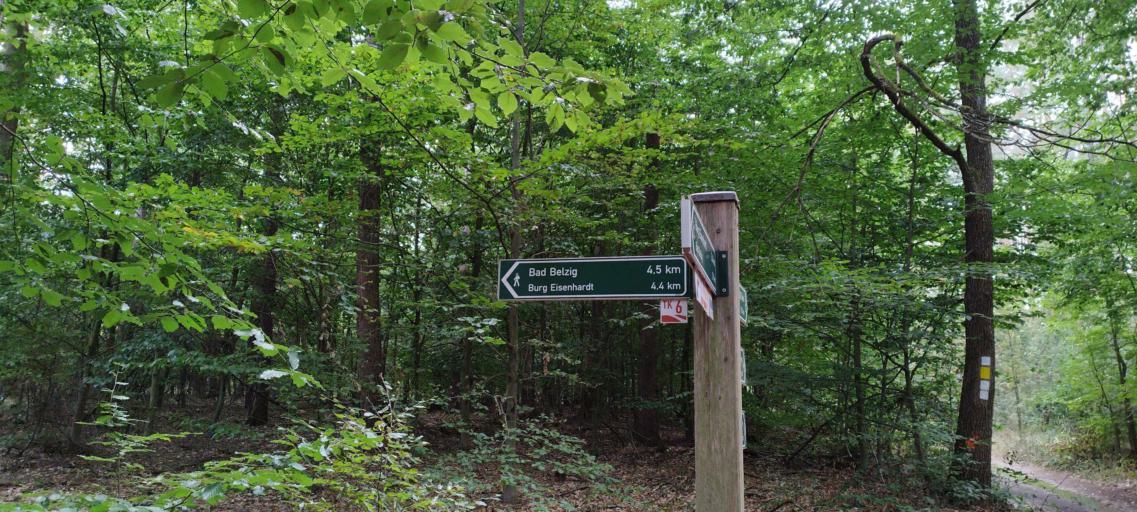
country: DE
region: Brandenburg
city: Belzig
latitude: 52.1442
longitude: 12.5449
